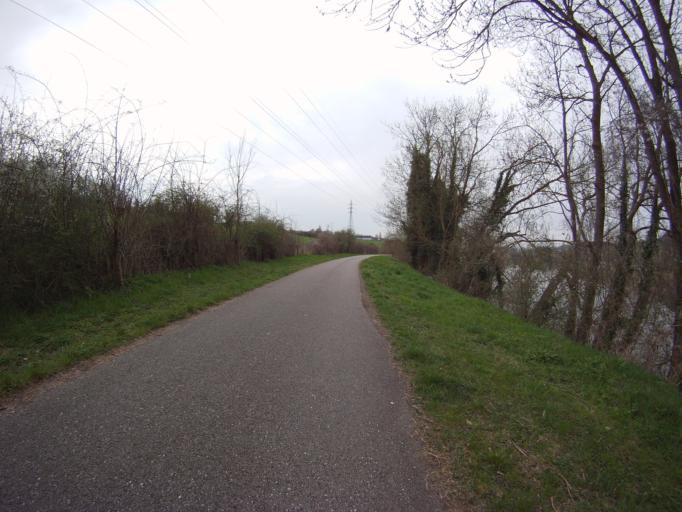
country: FR
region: Lorraine
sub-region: Departement de Meurthe-et-Moselle
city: Champigneulles
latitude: 48.7292
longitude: 6.1763
